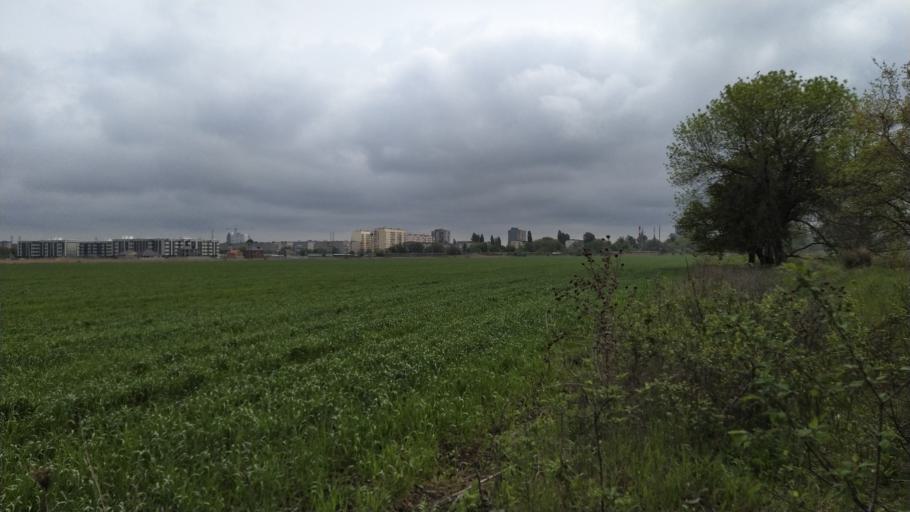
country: RU
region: Rostov
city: Bataysk
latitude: 47.1240
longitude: 39.7236
